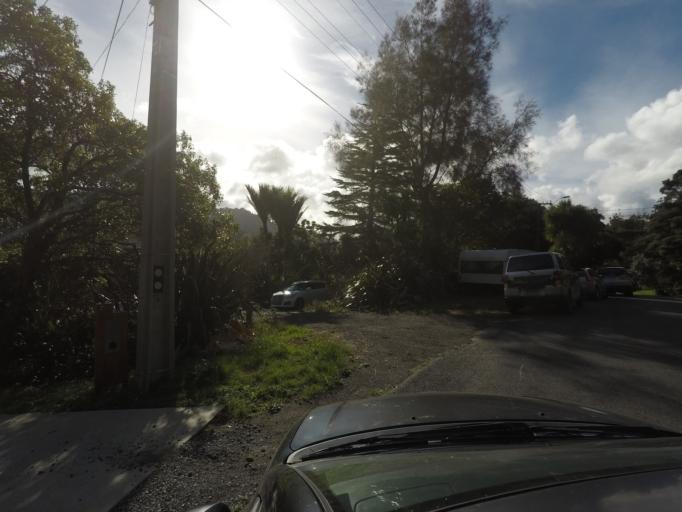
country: NZ
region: Auckland
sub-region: Auckland
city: Titirangi
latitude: -36.9984
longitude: 174.5759
